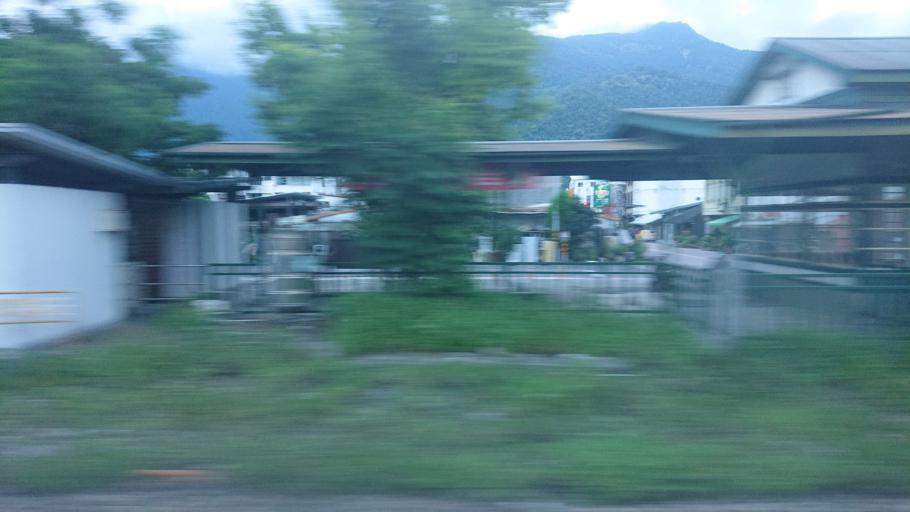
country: TW
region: Taiwan
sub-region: Taitung
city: Taitung
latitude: 23.0465
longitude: 121.1648
